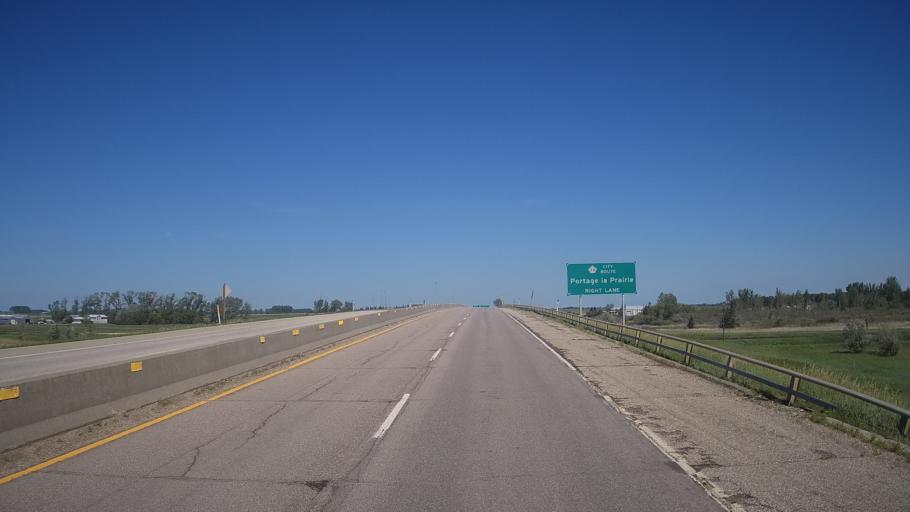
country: CA
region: Manitoba
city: Portage la Prairie
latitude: 49.9661
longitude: -98.3561
